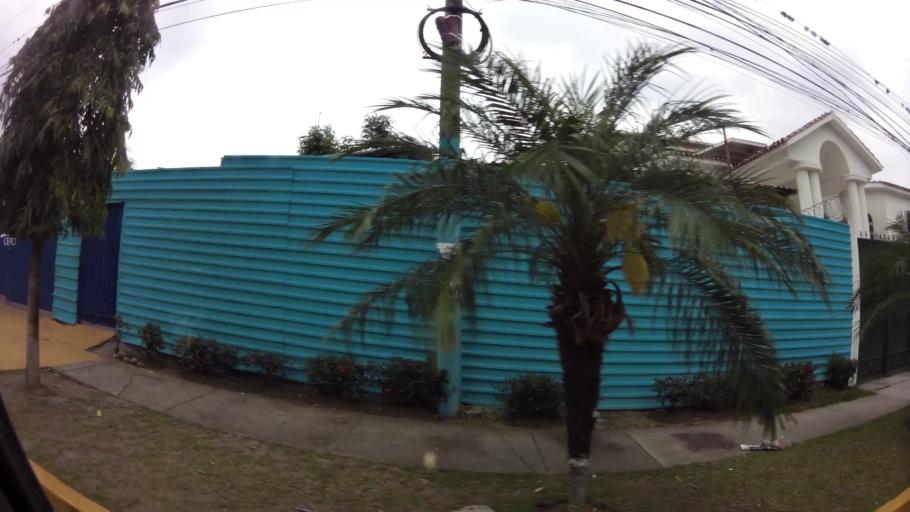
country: HN
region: Francisco Morazan
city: Tegucigalpa
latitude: 14.0759
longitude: -87.1806
